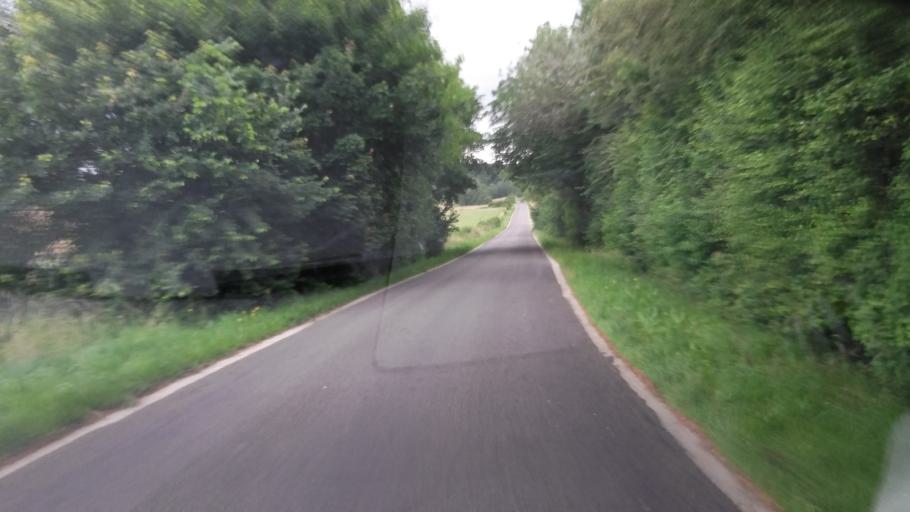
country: BE
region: Wallonia
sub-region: Province du Luxembourg
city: Arlon
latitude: 49.6683
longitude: 5.8415
